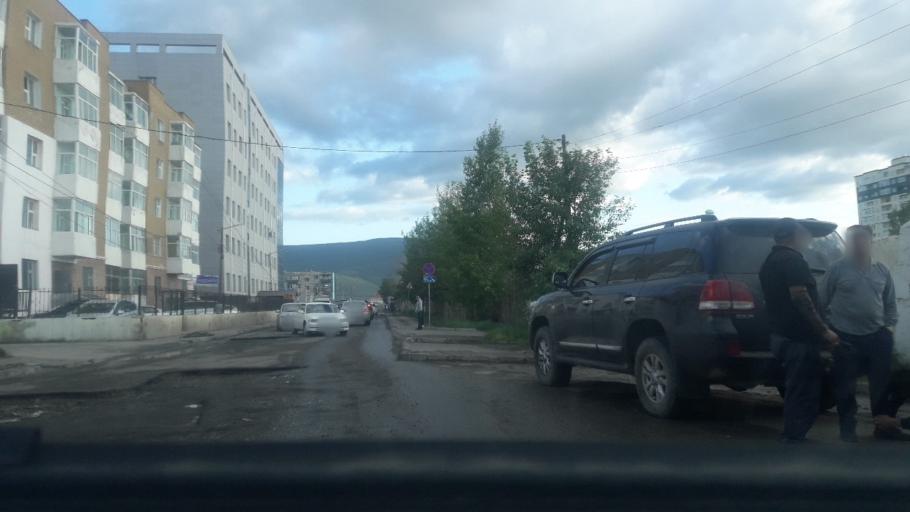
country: MN
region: Ulaanbaatar
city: Ulaanbaatar
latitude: 47.9159
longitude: 106.9945
